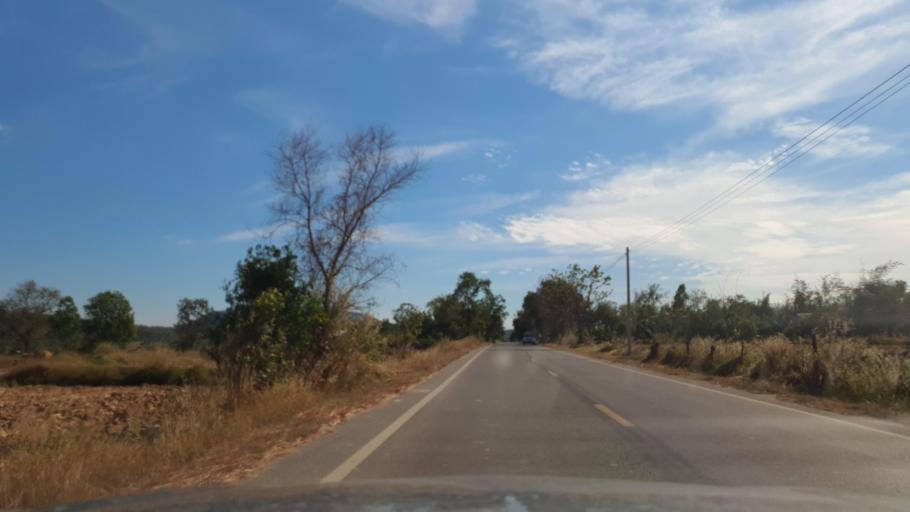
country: TH
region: Kalasin
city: Kuchinarai
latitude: 16.6025
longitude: 104.1352
